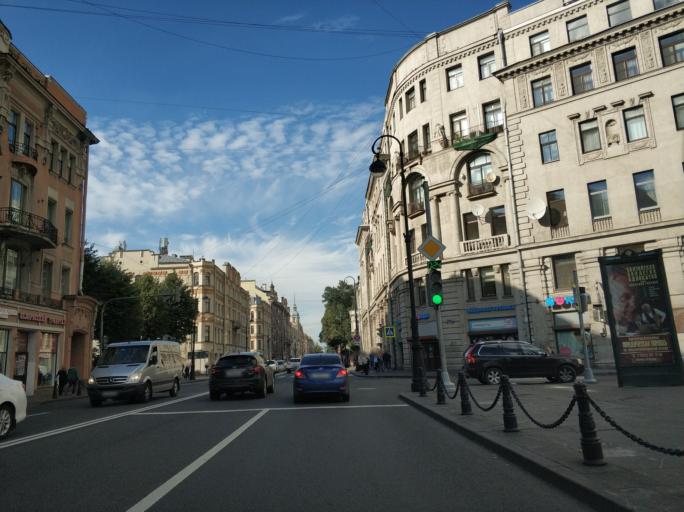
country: RU
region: St.-Petersburg
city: Petrogradka
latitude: 59.9579
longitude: 30.3194
